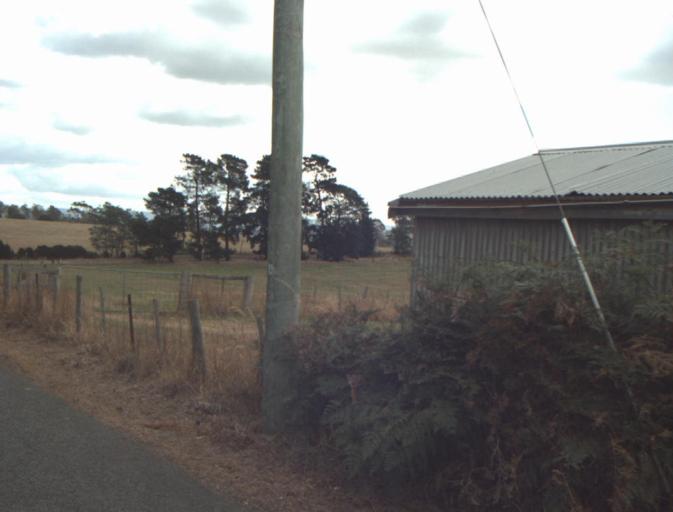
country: AU
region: Tasmania
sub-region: Launceston
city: Mayfield
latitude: -41.2933
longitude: 147.0103
